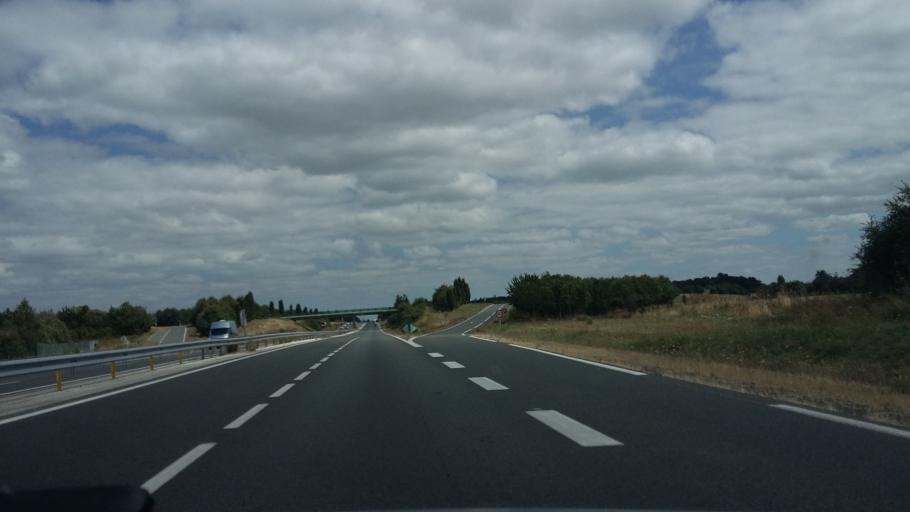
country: FR
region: Pays de la Loire
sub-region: Departement de la Vendee
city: La Chaize-le-Vicomte
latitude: 46.6541
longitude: -1.2341
